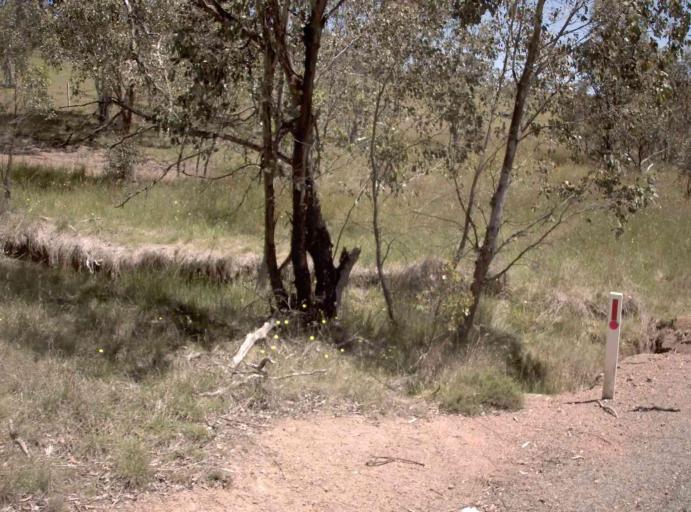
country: AU
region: New South Wales
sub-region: Snowy River
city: Jindabyne
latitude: -37.0629
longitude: 148.2616
